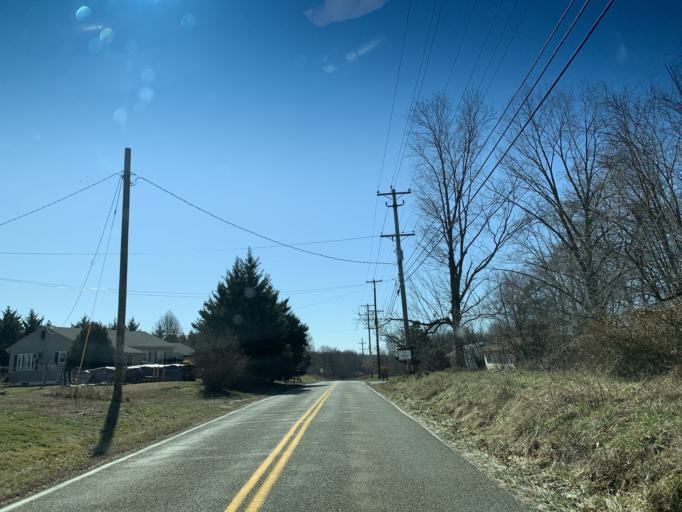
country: US
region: Maryland
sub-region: Cecil County
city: Elkton
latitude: 39.5133
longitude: -75.8270
